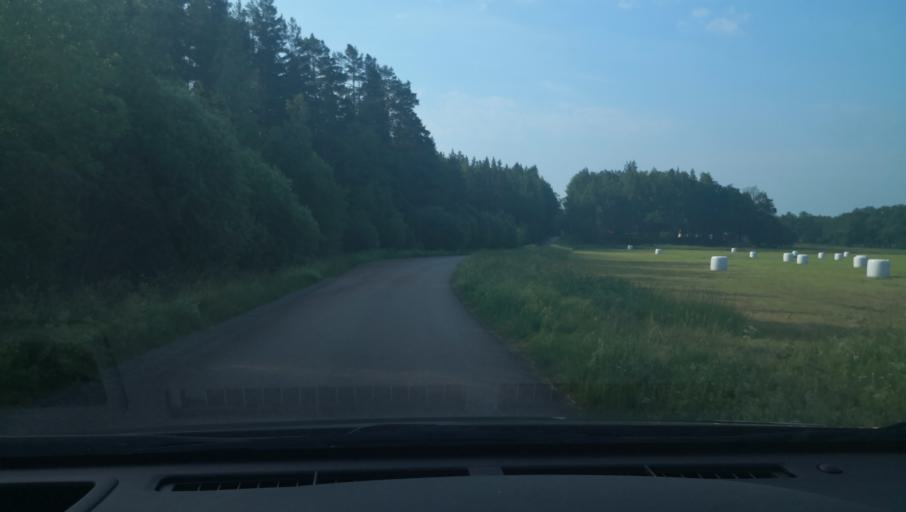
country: SE
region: Vaestmanland
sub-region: Arboga Kommun
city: Tyringe
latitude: 59.3917
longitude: 15.9432
